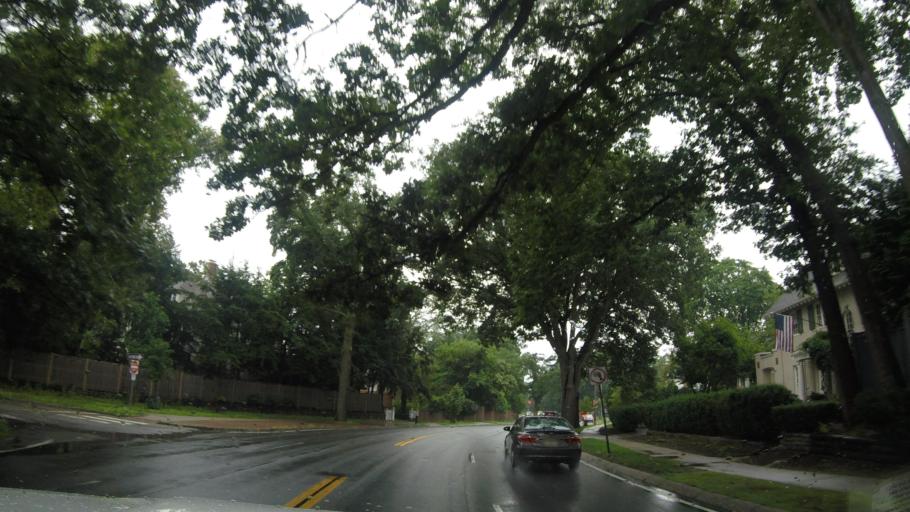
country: US
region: Massachusetts
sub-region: Middlesex County
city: Cambridge
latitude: 42.3773
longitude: -71.1419
